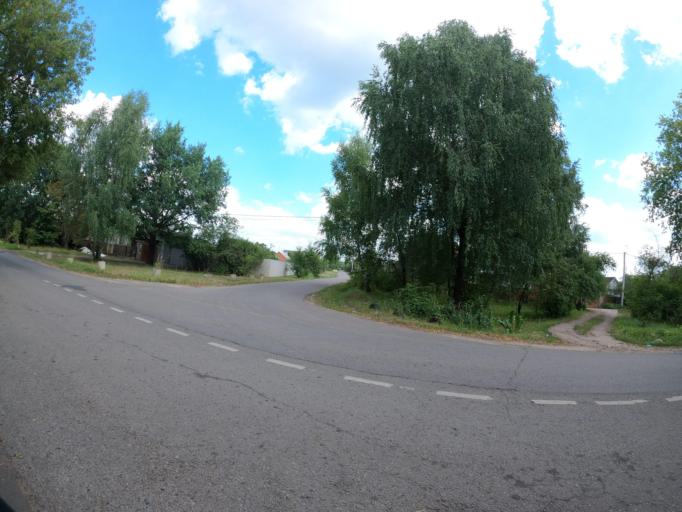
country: RU
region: Moskovskaya
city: Lopatinskiy
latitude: 55.2819
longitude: 38.7381
